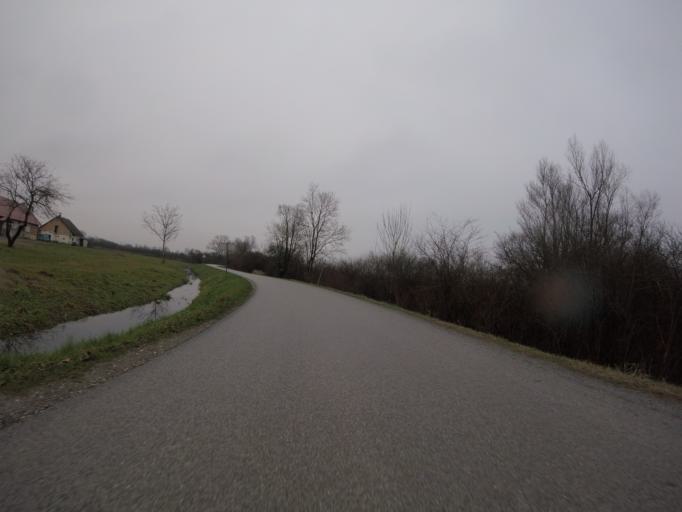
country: HR
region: Sisacko-Moslavacka
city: Lekenik
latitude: 45.6305
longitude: 16.3091
